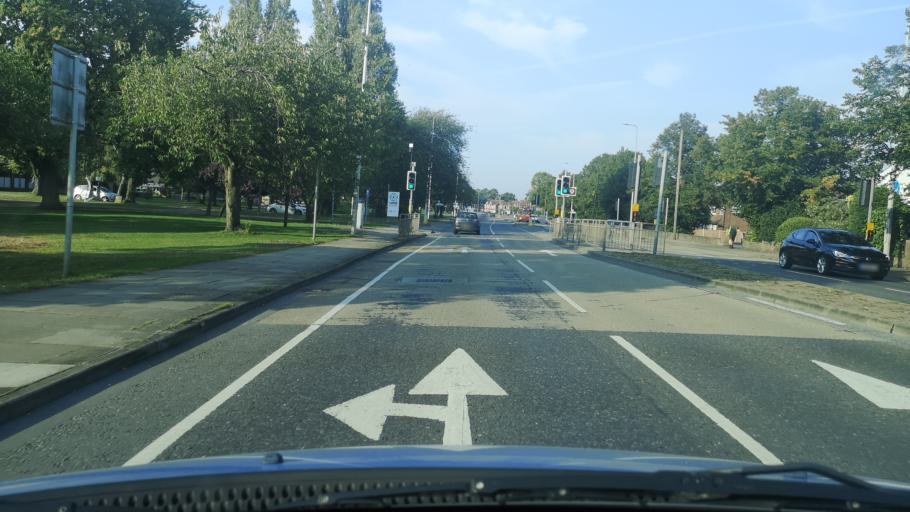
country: GB
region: England
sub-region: North Lincolnshire
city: Scunthorpe
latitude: 53.5800
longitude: -0.6545
